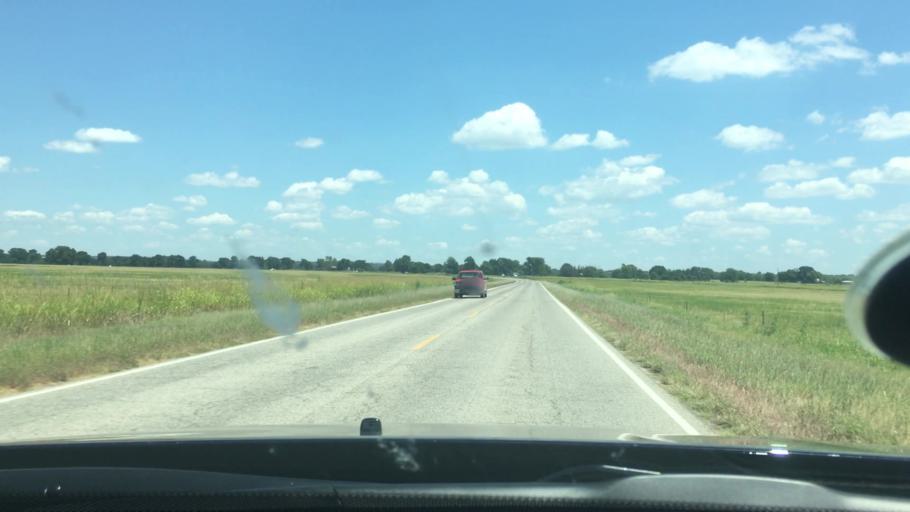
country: US
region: Oklahoma
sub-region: Carter County
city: Dickson
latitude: 34.2472
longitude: -96.9715
